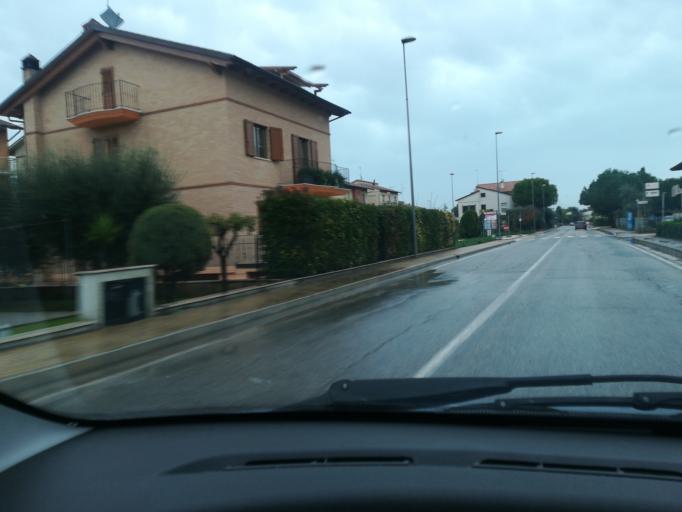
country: IT
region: The Marches
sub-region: Provincia di Macerata
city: Borgo Stazione
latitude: 43.2824
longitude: 13.6334
